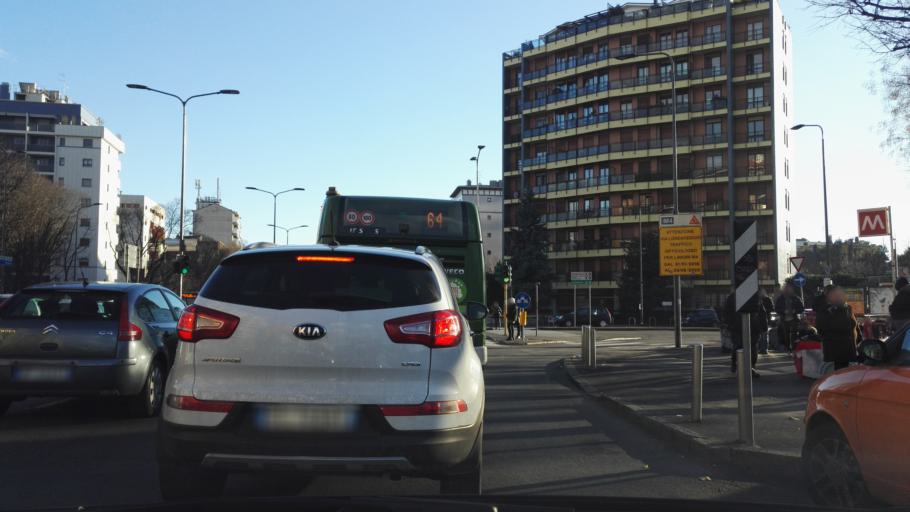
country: IT
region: Lombardy
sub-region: Citta metropolitana di Milano
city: Romano Banco
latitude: 45.4599
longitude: 9.1294
